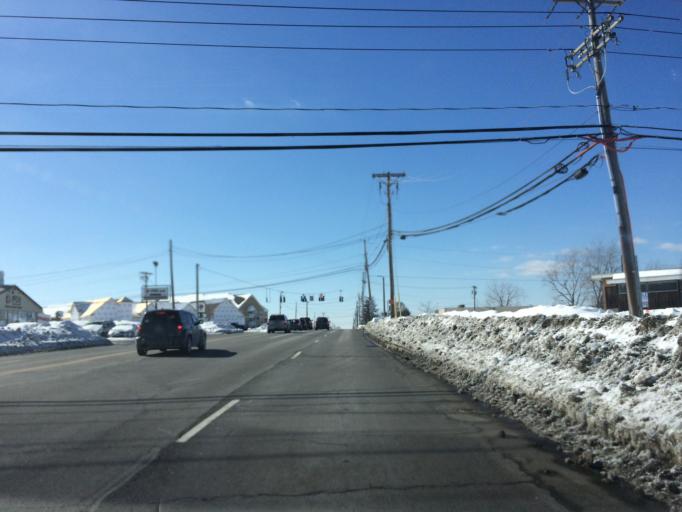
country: US
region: New York
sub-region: Monroe County
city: Rochester
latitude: 43.0949
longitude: -77.6120
